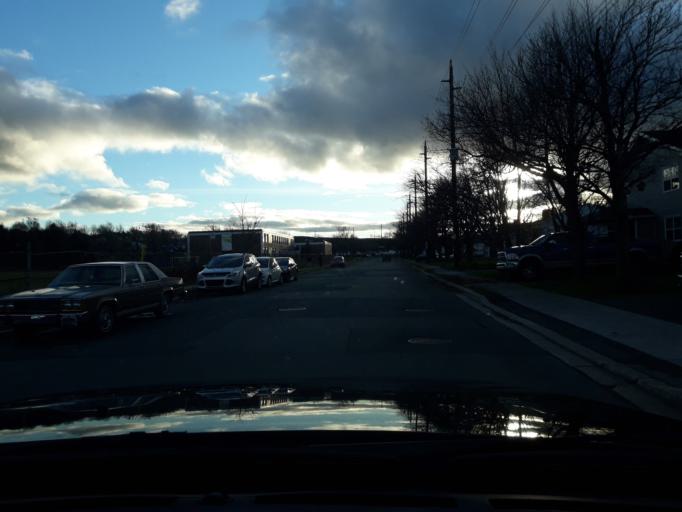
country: CA
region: Newfoundland and Labrador
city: St. John's
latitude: 47.5696
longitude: -52.7398
